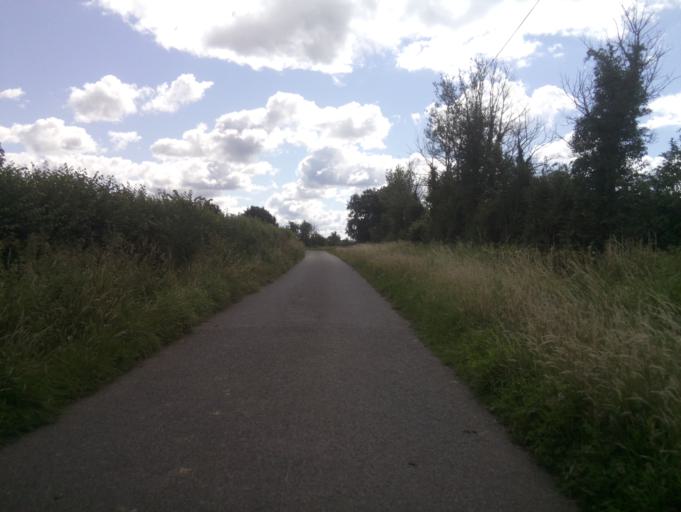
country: GB
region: England
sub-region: Gloucestershire
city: Newent
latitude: 51.8503
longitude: -2.3655
